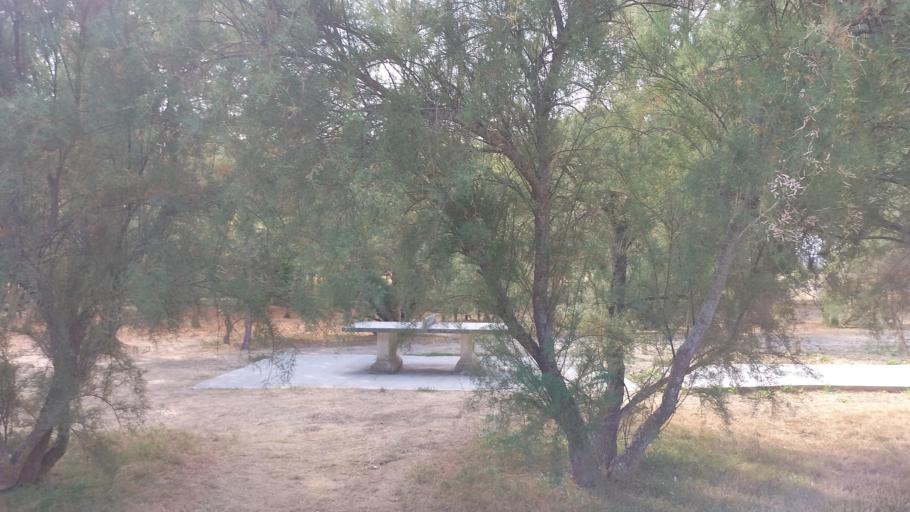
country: FR
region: Poitou-Charentes
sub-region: Departement de la Charente-Maritime
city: Saint-Denis-d'Oleron
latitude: 45.9745
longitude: -1.3366
